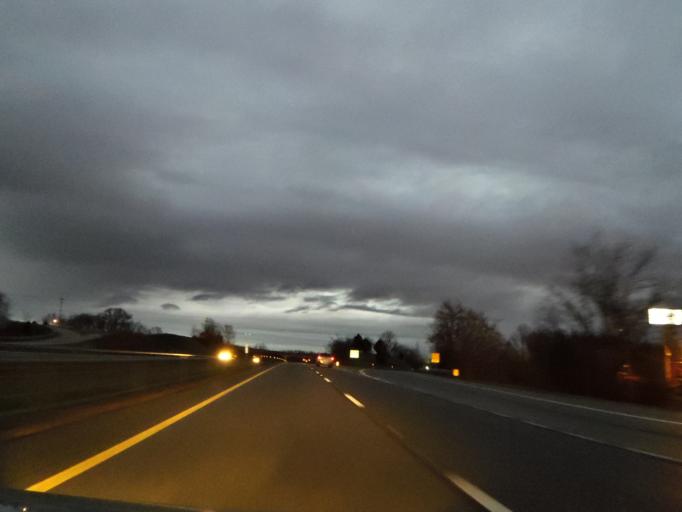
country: US
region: Tennessee
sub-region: Washington County
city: Gray
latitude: 36.4324
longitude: -82.5200
